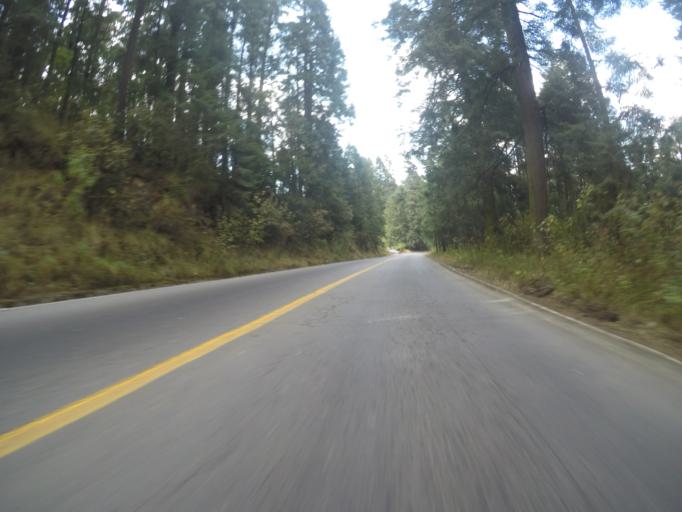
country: MX
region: Mexico
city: Cerro La Calera
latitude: 19.1850
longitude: -99.8062
